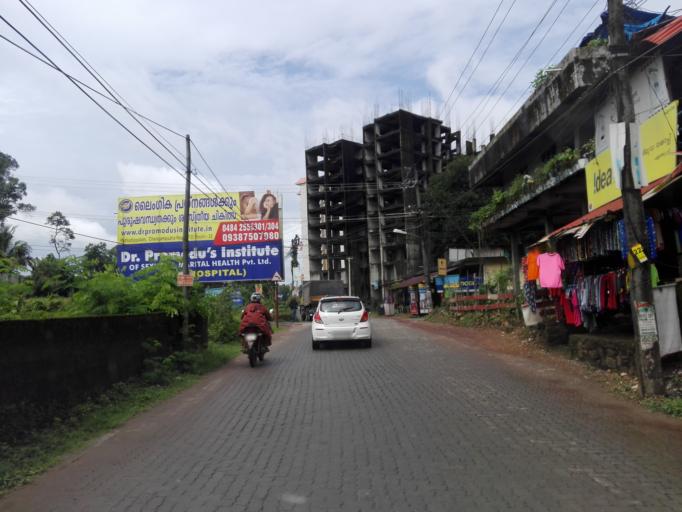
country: IN
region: Kerala
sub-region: Ernakulam
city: Aluva
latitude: 10.0262
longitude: 76.3577
